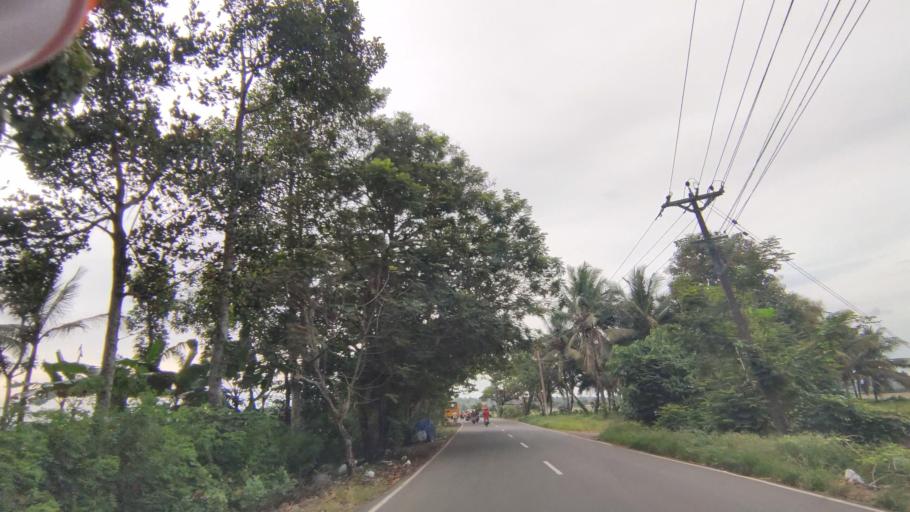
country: IN
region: Kerala
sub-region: Kottayam
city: Kottayam
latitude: 9.6904
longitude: 76.4971
